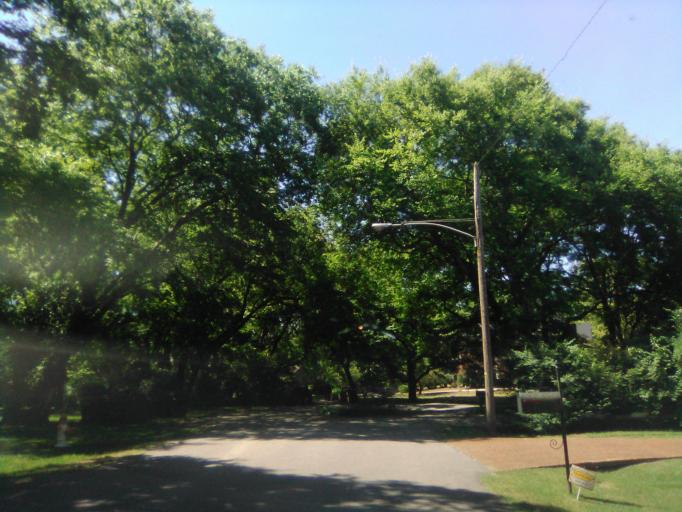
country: US
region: Tennessee
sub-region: Davidson County
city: Belle Meade
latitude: 36.1214
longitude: -86.8402
